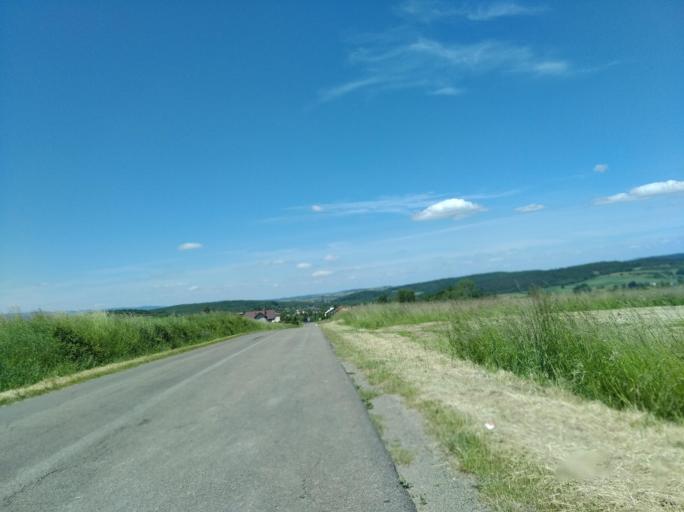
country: PL
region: Subcarpathian Voivodeship
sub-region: Powiat krosnienski
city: Chorkowka
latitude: 49.6419
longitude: 21.6206
